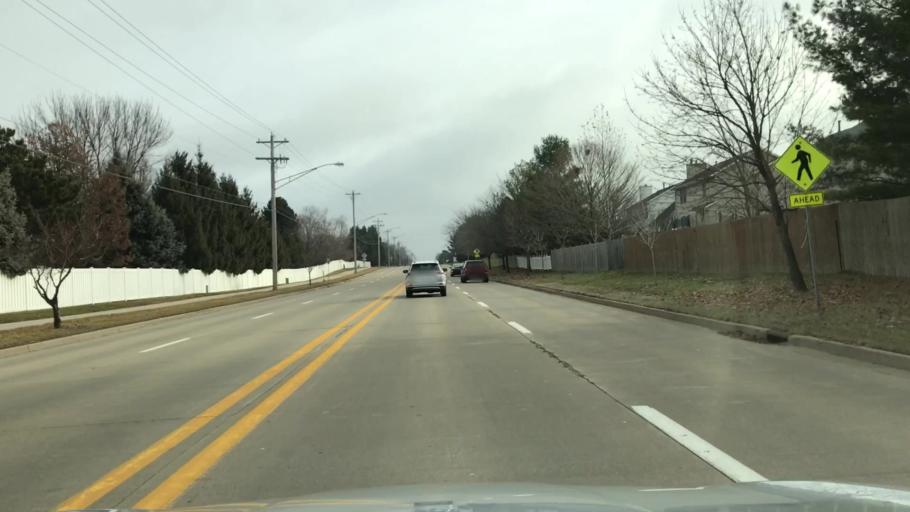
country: US
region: Illinois
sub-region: McLean County
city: Normal
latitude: 40.5026
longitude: -88.9155
